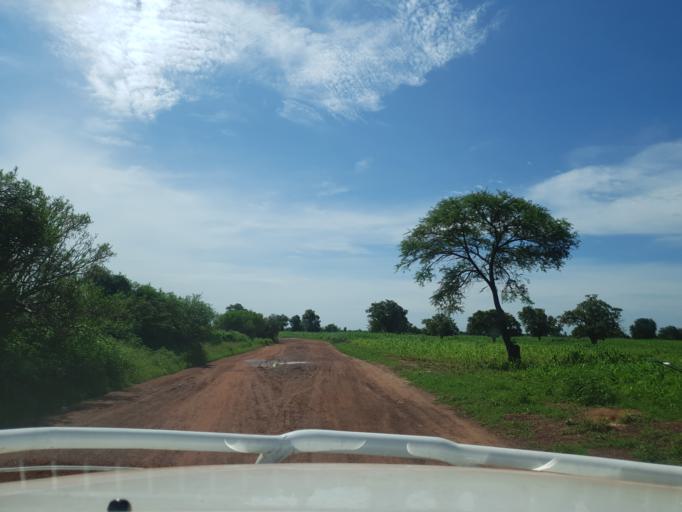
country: ML
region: Koulikoro
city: Banamba
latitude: 13.2768
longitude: -7.5472
